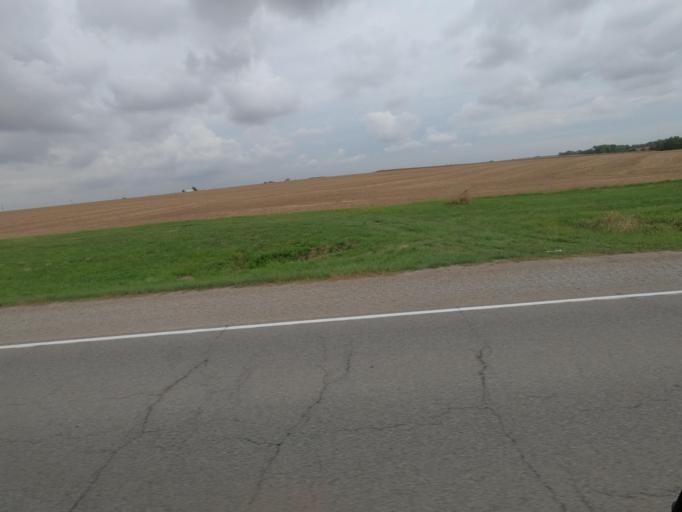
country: US
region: Iowa
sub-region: Wapello County
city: Ottumwa
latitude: 40.9760
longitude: -92.2366
